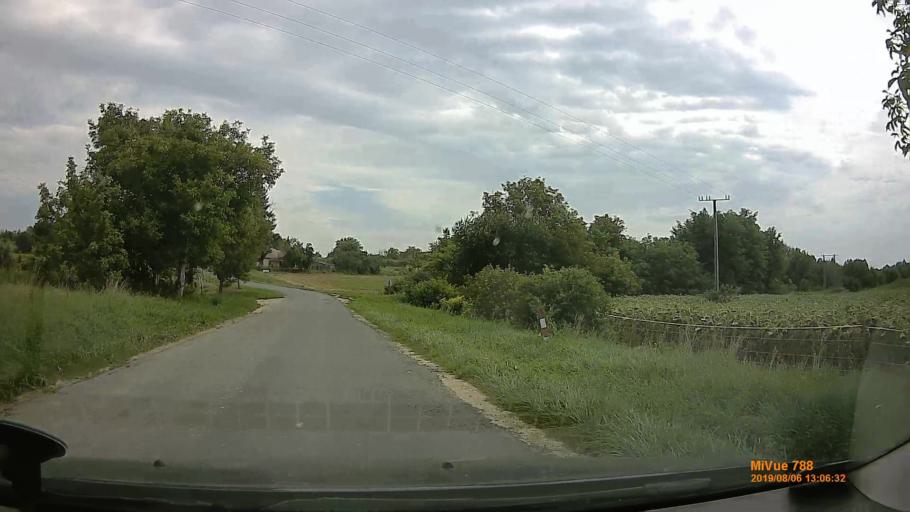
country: HU
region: Zala
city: Pacsa
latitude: 46.6300
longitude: 17.0535
